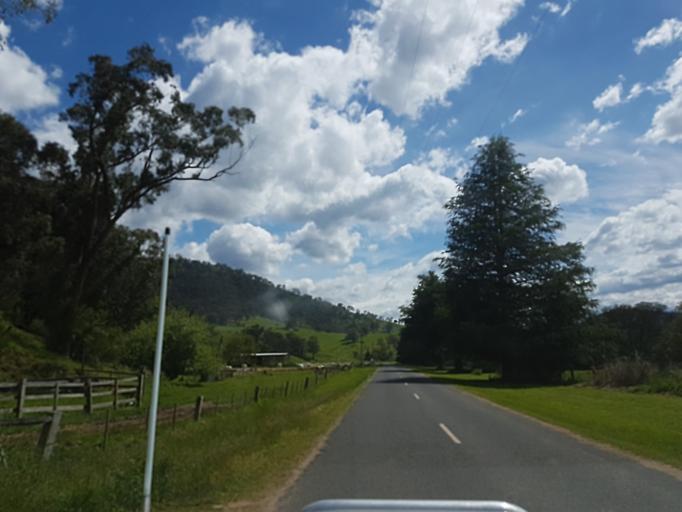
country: AU
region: Victoria
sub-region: East Gippsland
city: Bairnsdale
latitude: -37.4517
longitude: 147.2471
